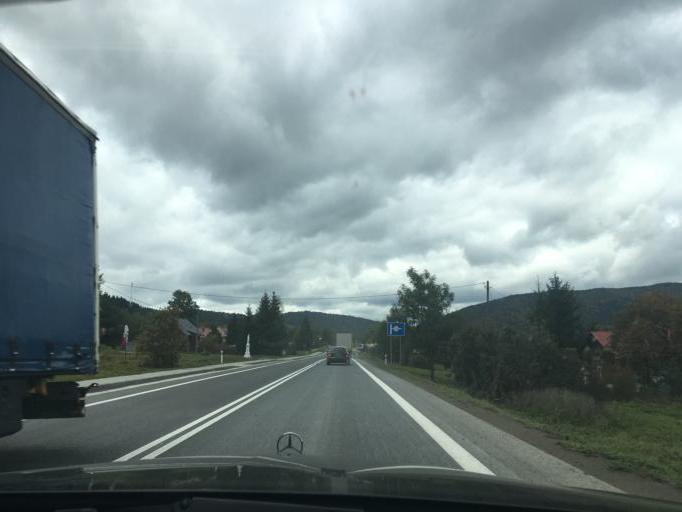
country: PL
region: Subcarpathian Voivodeship
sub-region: Powiat krosnienski
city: Dukla
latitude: 49.4988
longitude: 21.7004
